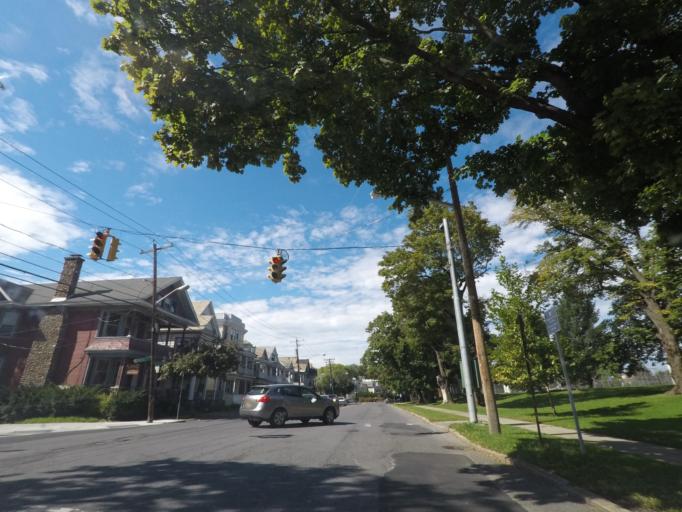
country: US
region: New York
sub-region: Albany County
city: Albany
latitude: 42.6451
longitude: -73.7699
